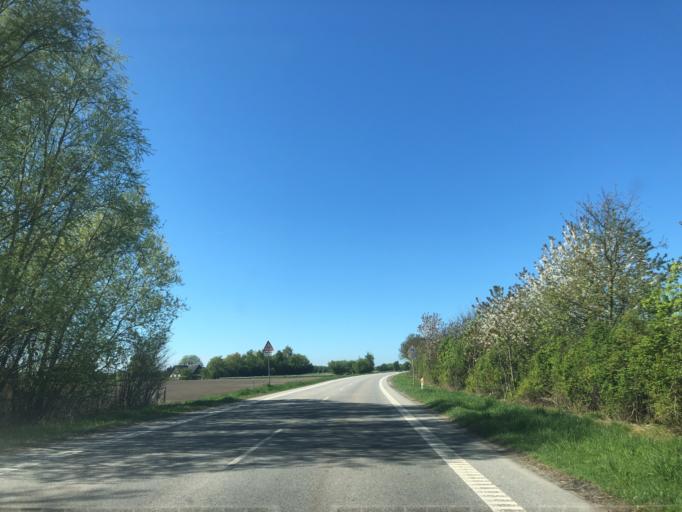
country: DK
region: Zealand
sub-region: Stevns Kommune
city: Store Heddinge
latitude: 55.3041
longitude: 12.3737
